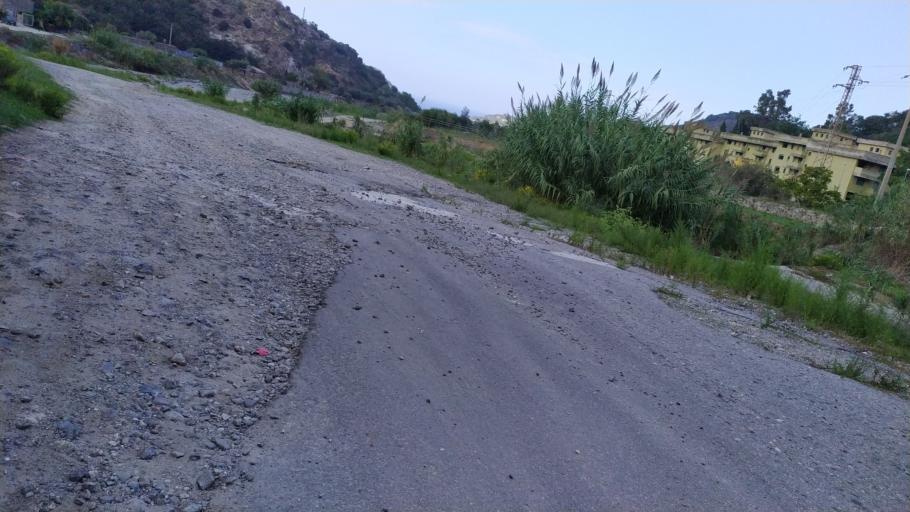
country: IT
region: Sicily
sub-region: Messina
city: Saponara
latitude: 38.1950
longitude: 15.4300
